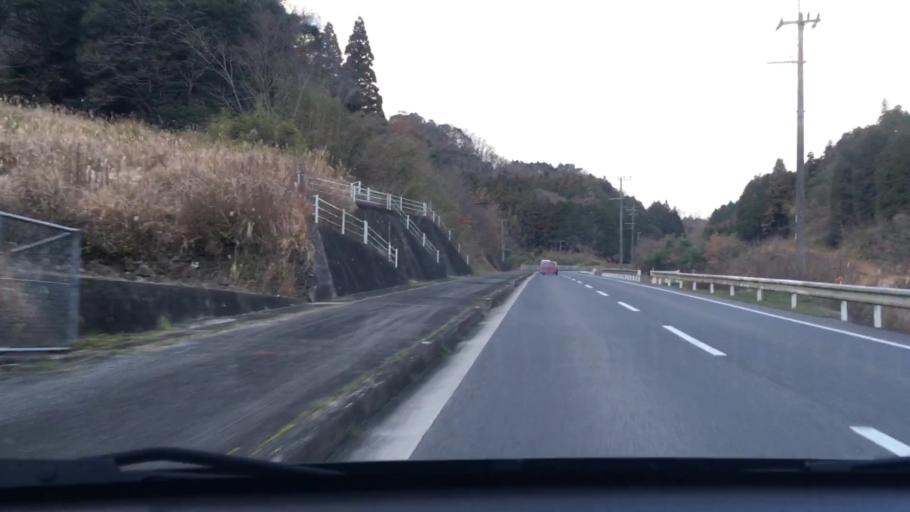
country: JP
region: Oita
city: Bungo-Takada-shi
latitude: 33.4716
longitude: 131.3845
